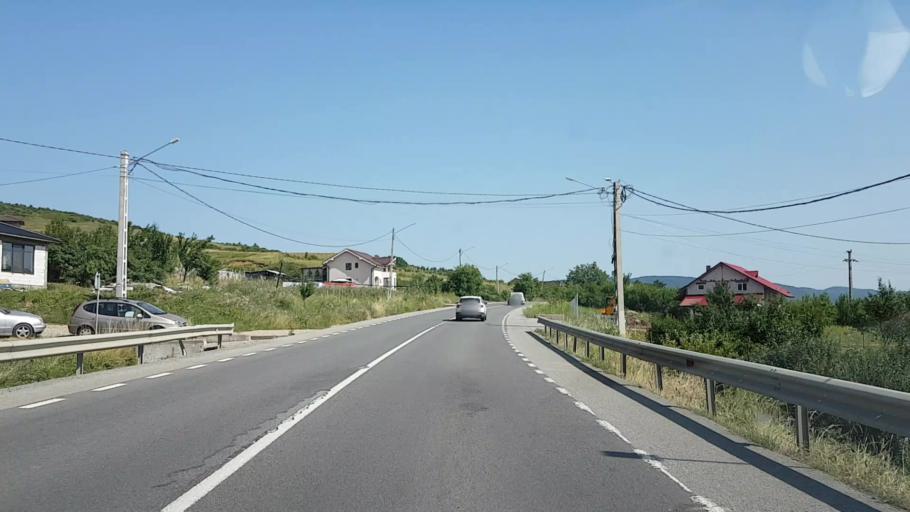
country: RO
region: Bistrita-Nasaud
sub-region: Comuna Sieu-Magherus
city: Sieu-Magherus
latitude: 47.0782
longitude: 24.3961
